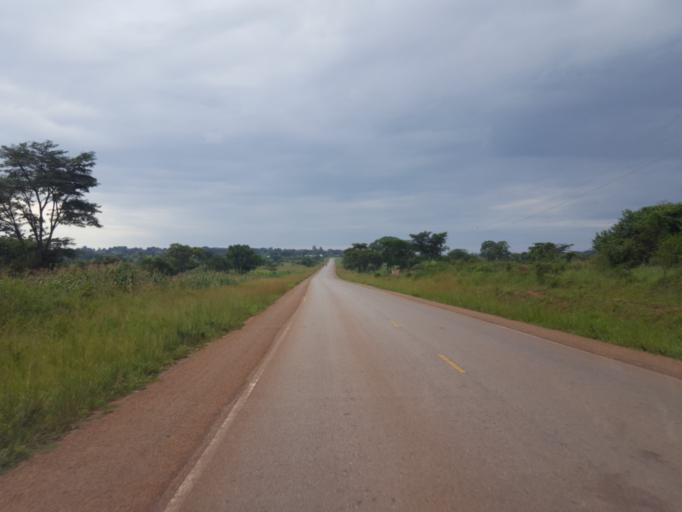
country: UG
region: Central Region
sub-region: Kyankwanzi District
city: Kyankwanzi
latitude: 1.0823
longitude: 31.6389
